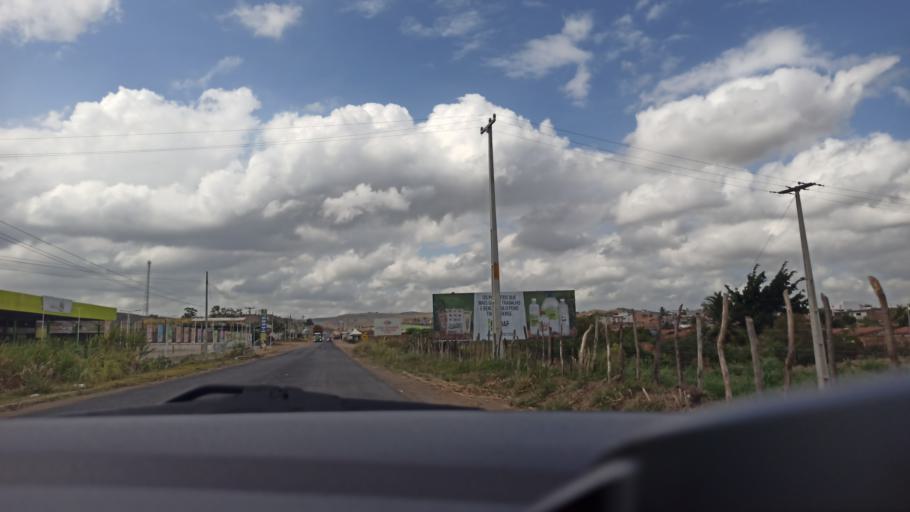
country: BR
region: Pernambuco
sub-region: Timbauba
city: Timbauba
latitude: -7.4923
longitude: -35.2970
